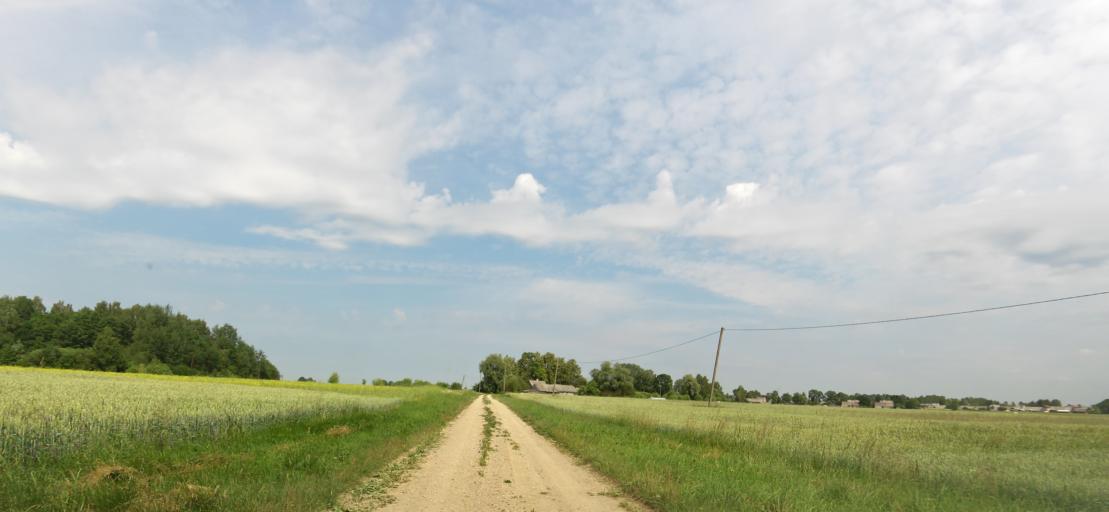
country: LT
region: Panevezys
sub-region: Birzai
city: Birzai
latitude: 56.3213
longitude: 24.7000
